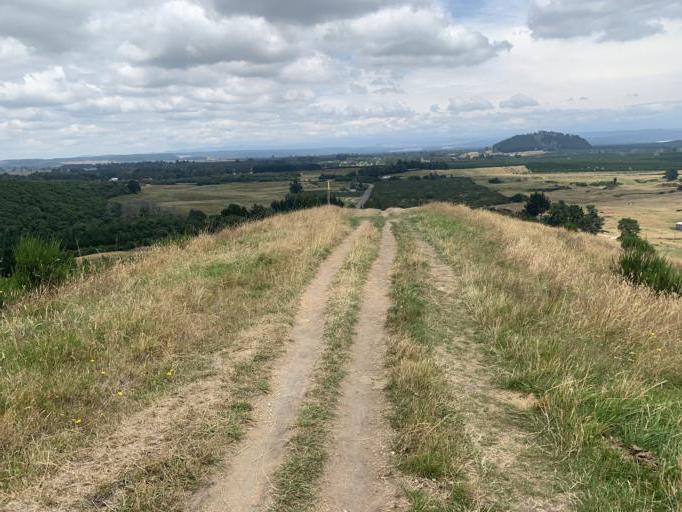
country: NZ
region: Waikato
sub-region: Taupo District
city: Taupo
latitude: -38.7011
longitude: 176.1422
